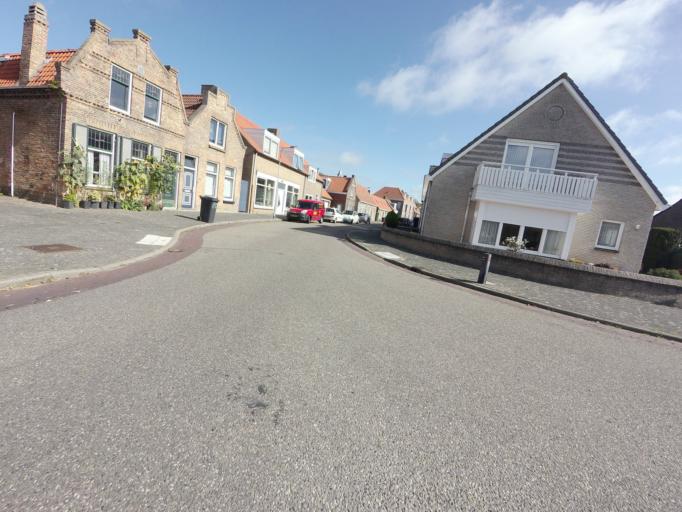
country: NL
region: Zeeland
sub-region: Gemeente Vlissingen
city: Vlissingen
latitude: 51.4810
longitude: 3.5529
